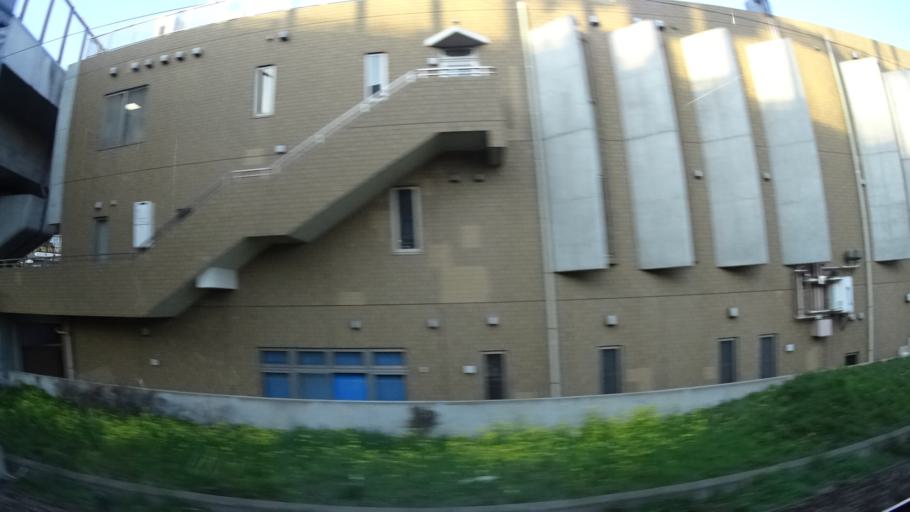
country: JP
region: Kanagawa
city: Yokohama
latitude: 35.3955
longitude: 139.6091
